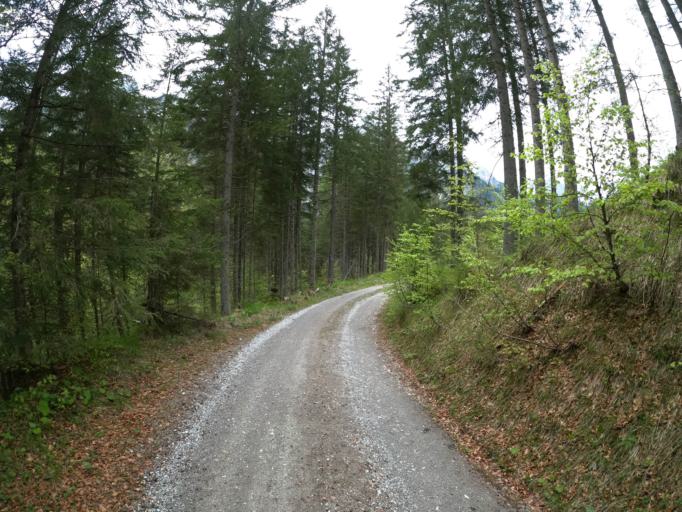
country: AT
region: Salzburg
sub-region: Politischer Bezirk Zell am See
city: Dienten am Hochkonig
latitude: 47.4706
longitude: 13.0546
